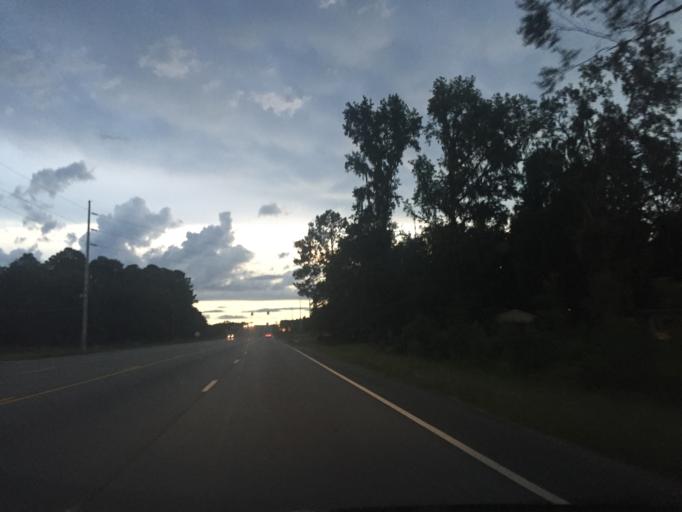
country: US
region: Georgia
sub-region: Liberty County
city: Hinesville
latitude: 31.8310
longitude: -81.5304
